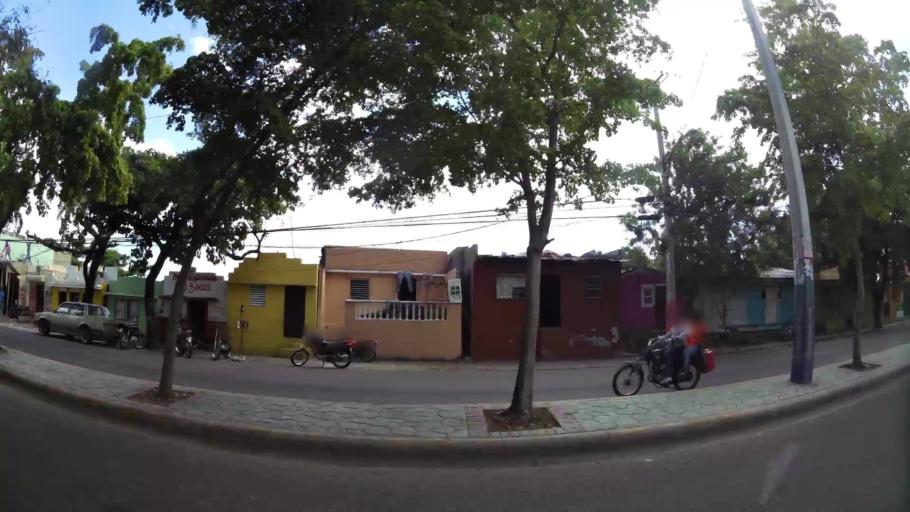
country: DO
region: Nacional
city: Ensanche Luperon
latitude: 18.4931
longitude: -69.8834
